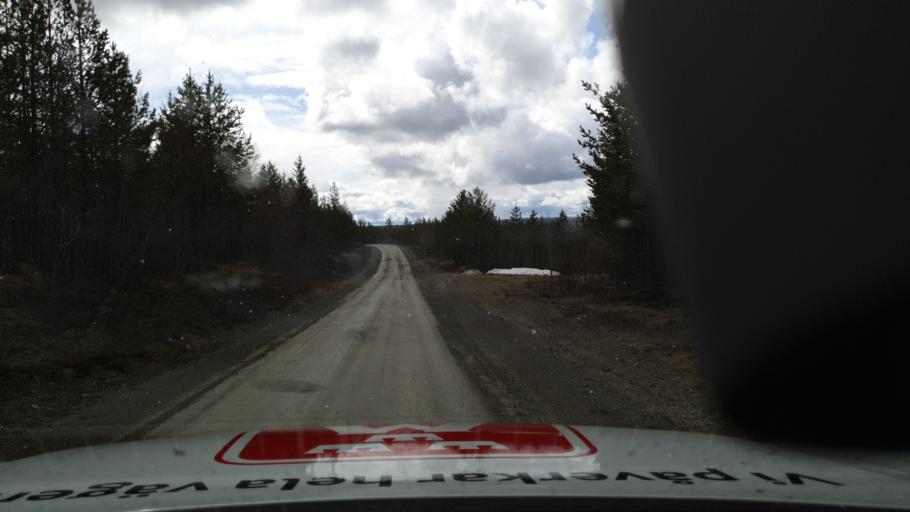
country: SE
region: Jaemtland
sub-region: Bergs Kommun
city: Hoverberg
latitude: 62.7764
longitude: 13.8270
